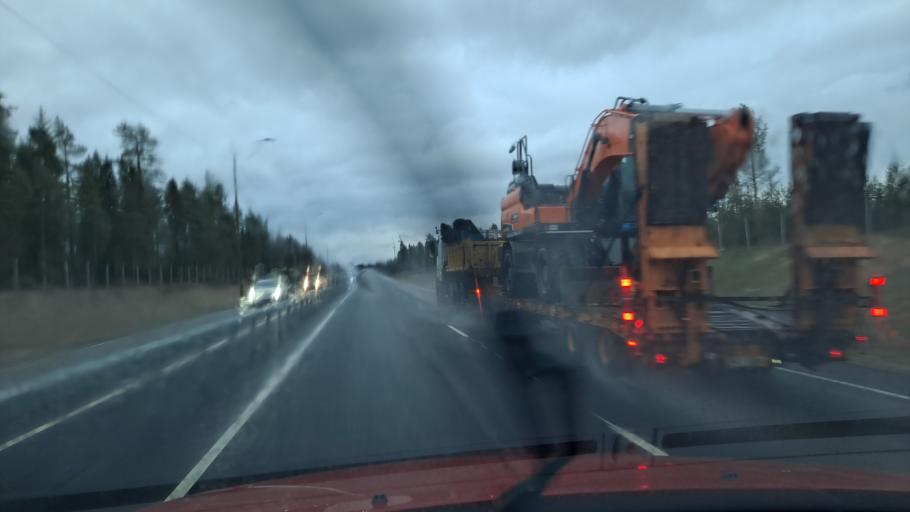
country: FI
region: Lapland
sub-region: Kemi-Tornio
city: Simo
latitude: 65.6530
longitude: 25.0909
